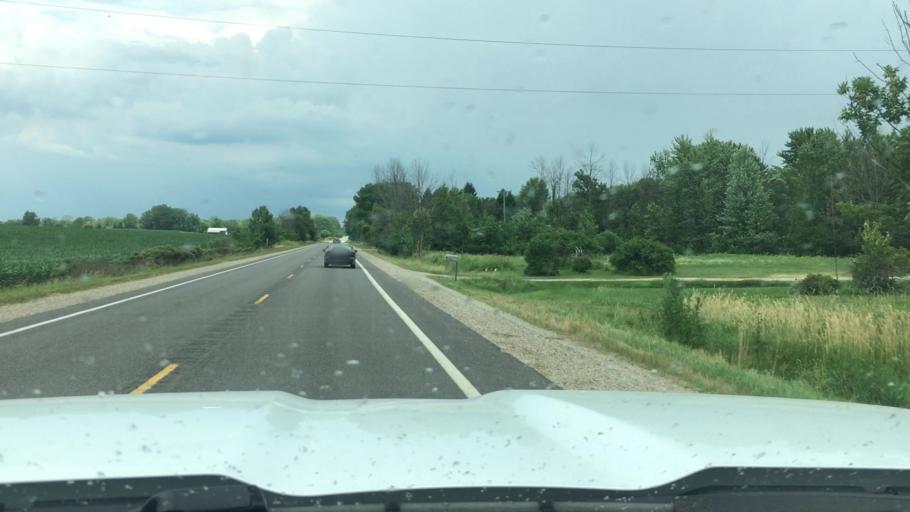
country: US
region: Michigan
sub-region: Montcalm County
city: Stanton
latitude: 43.1775
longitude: -85.0247
